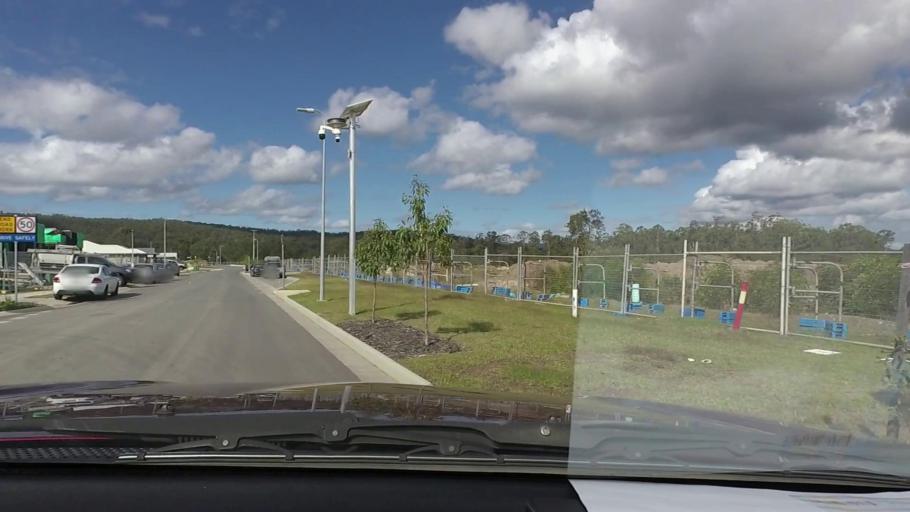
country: AU
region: Queensland
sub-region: Logan
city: Chambers Flat
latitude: -27.8095
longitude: 153.1226
